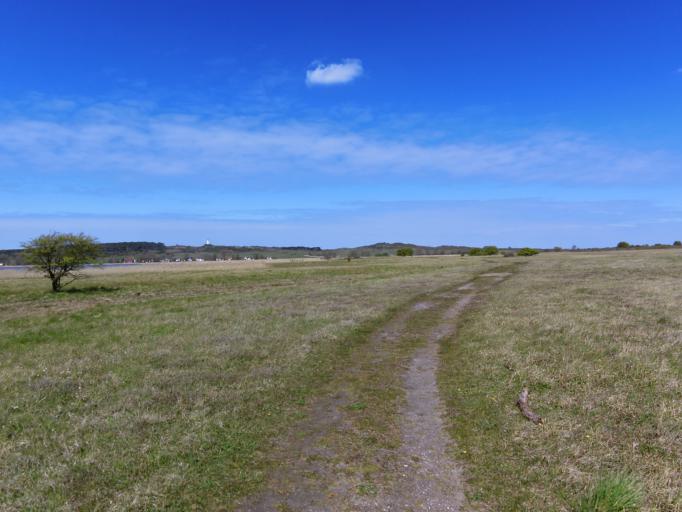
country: DE
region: Mecklenburg-Vorpommern
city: Hiddensee
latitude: 54.5841
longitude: 13.1428
